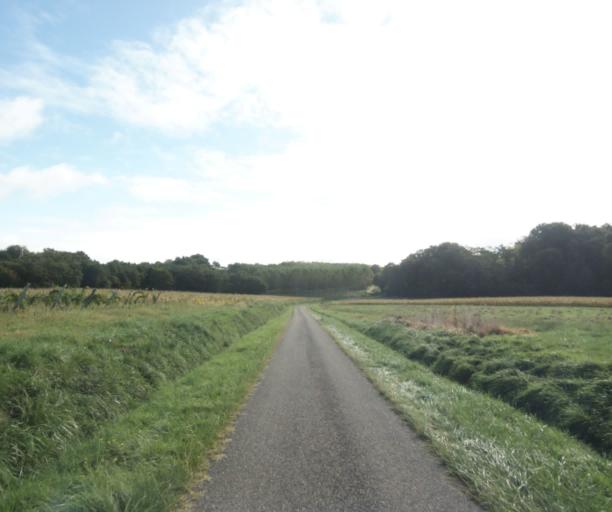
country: FR
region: Midi-Pyrenees
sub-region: Departement du Gers
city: Cazaubon
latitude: 43.8507
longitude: -0.0480
